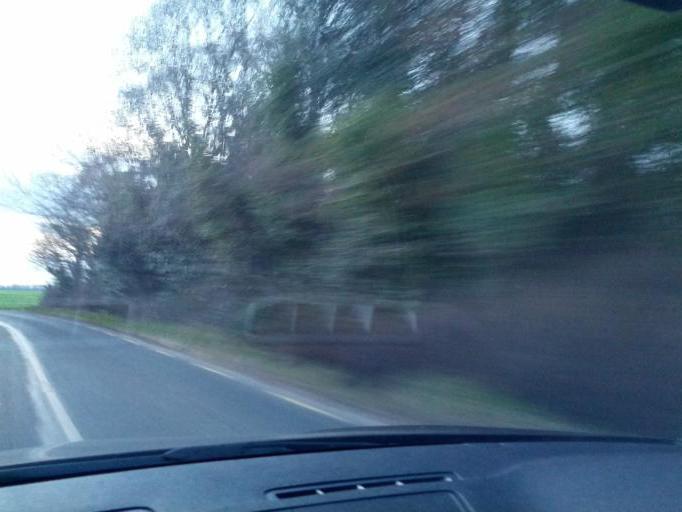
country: IE
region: Leinster
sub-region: Uibh Fhaili
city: Banagher
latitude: 53.1063
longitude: -8.0620
